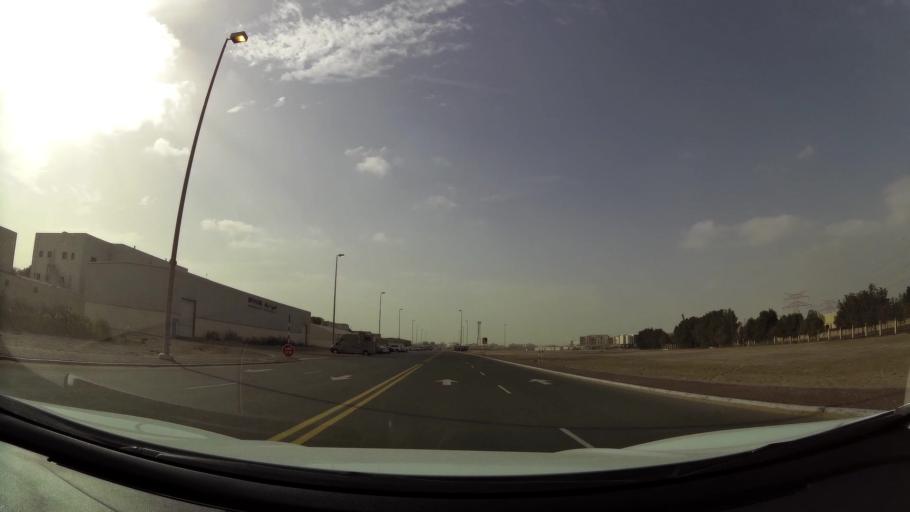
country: AE
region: Abu Dhabi
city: Abu Dhabi
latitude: 24.4093
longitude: 54.5195
